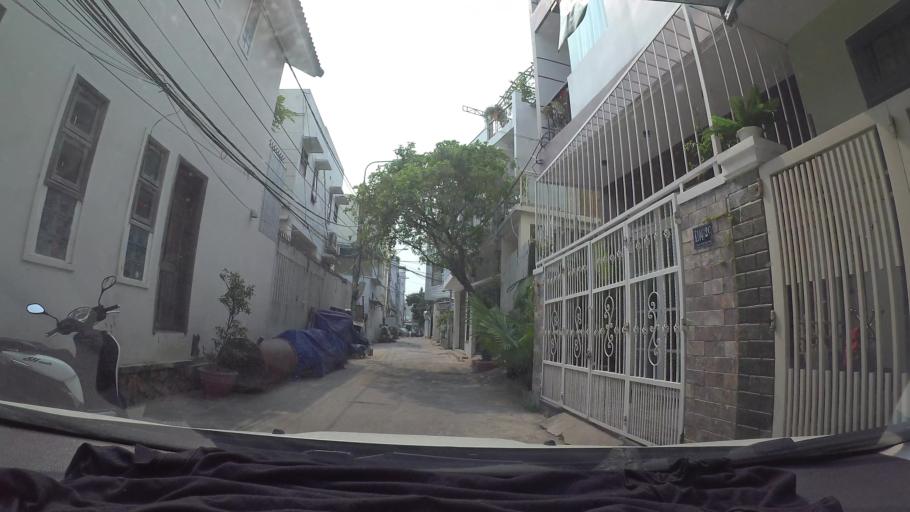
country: VN
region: Da Nang
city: Son Tra
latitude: 16.0412
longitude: 108.2172
